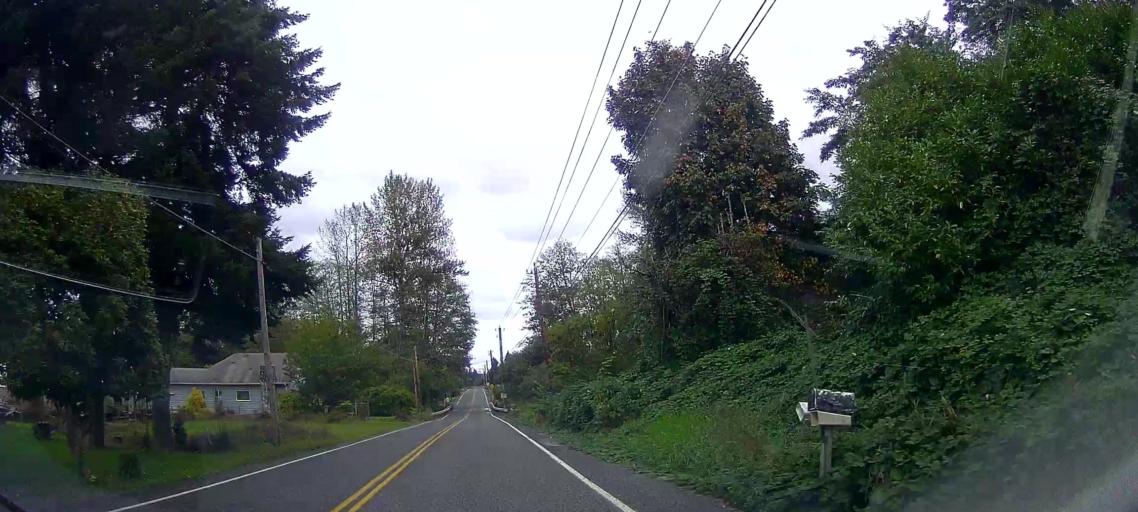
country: US
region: Washington
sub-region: Skagit County
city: Sedro-Woolley
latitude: 48.5264
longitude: -122.0933
